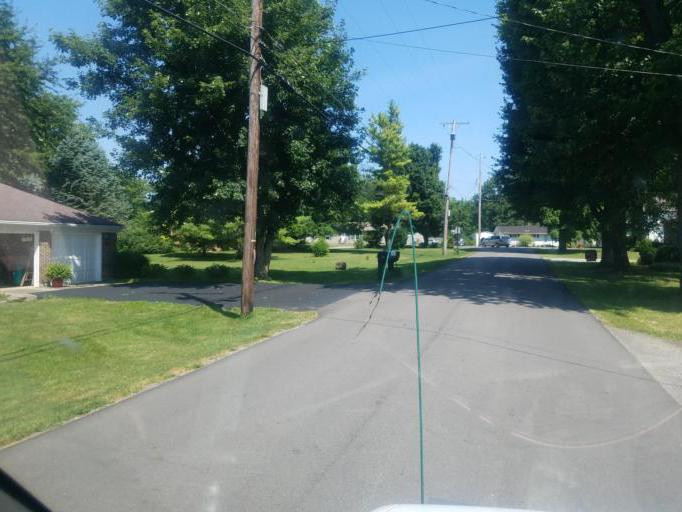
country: US
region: Ohio
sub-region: Champaign County
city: North Lewisburg
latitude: 40.2272
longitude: -83.5547
